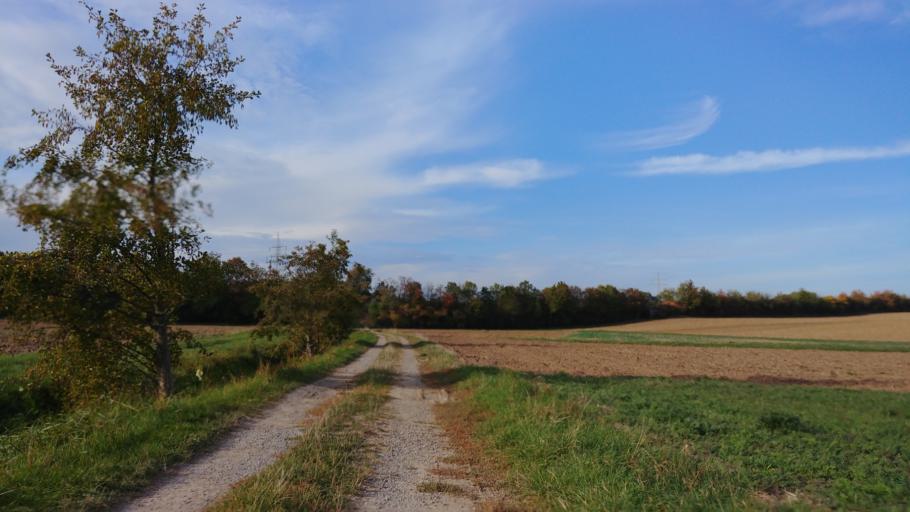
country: DE
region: Baden-Wuerttemberg
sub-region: Regierungsbezirk Stuttgart
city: Abstatt
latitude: 49.0610
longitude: 9.2747
